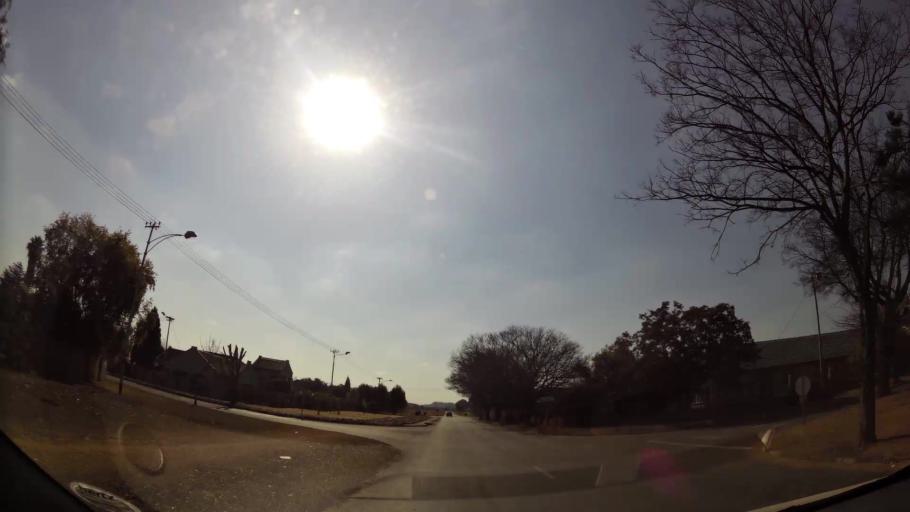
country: ZA
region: Gauteng
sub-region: West Rand District Municipality
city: Randfontein
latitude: -26.1550
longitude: 27.6918
